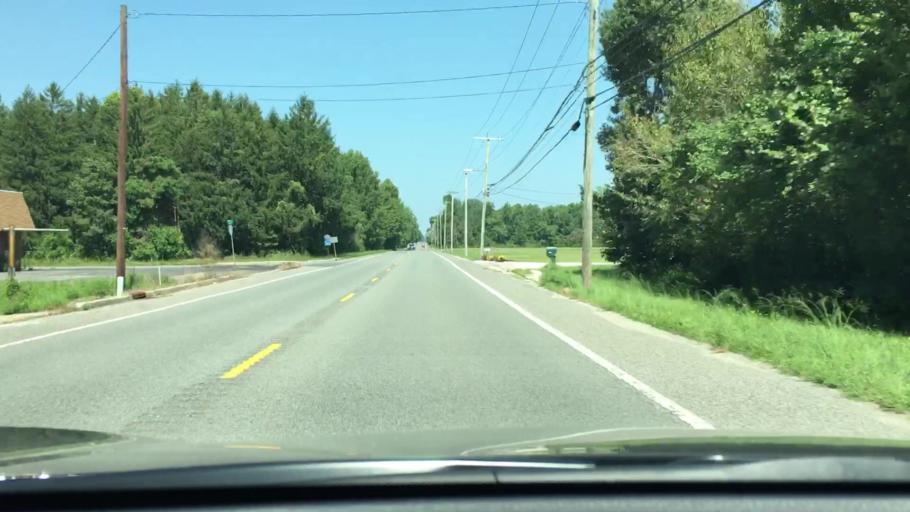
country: US
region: New Jersey
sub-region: Cumberland County
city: Laurel Lake
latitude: 39.2985
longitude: -75.0005
